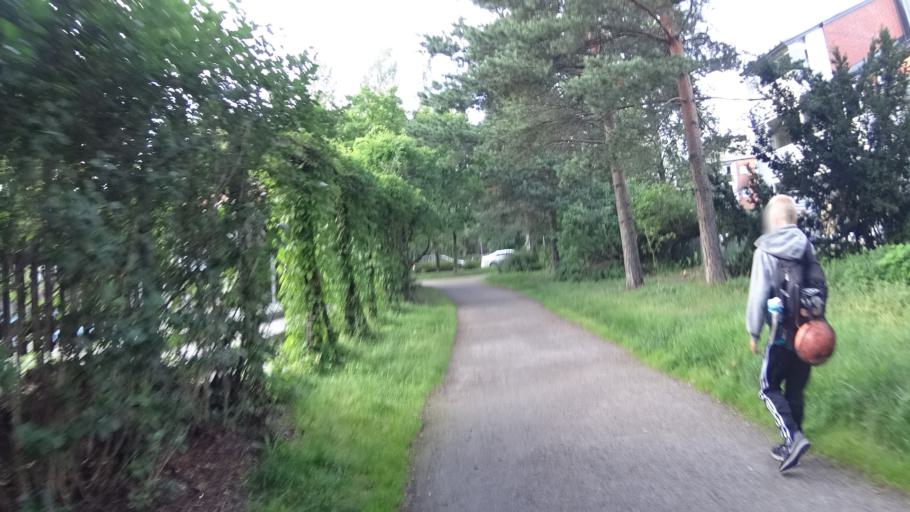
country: FI
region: Uusimaa
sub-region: Helsinki
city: Teekkarikylae
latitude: 60.2320
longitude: 24.8782
